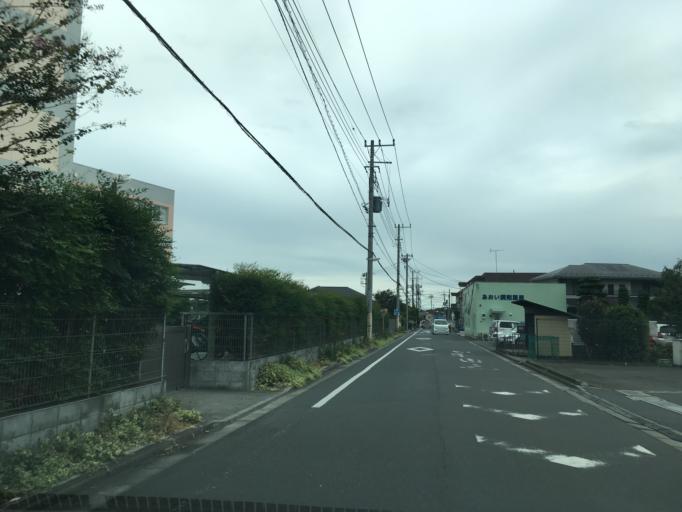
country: JP
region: Saitama
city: Tokorozawa
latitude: 35.8099
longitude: 139.4281
